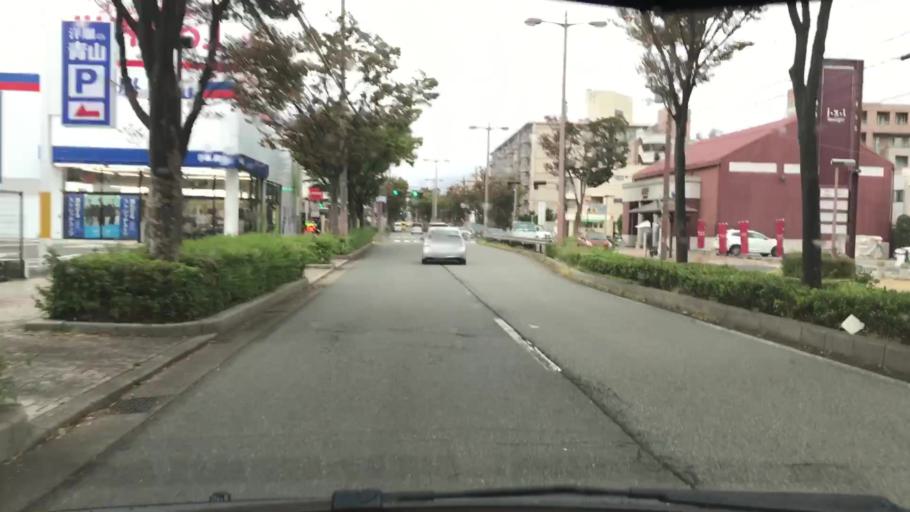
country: JP
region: Hyogo
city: Amagasaki
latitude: 34.7446
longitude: 135.3918
